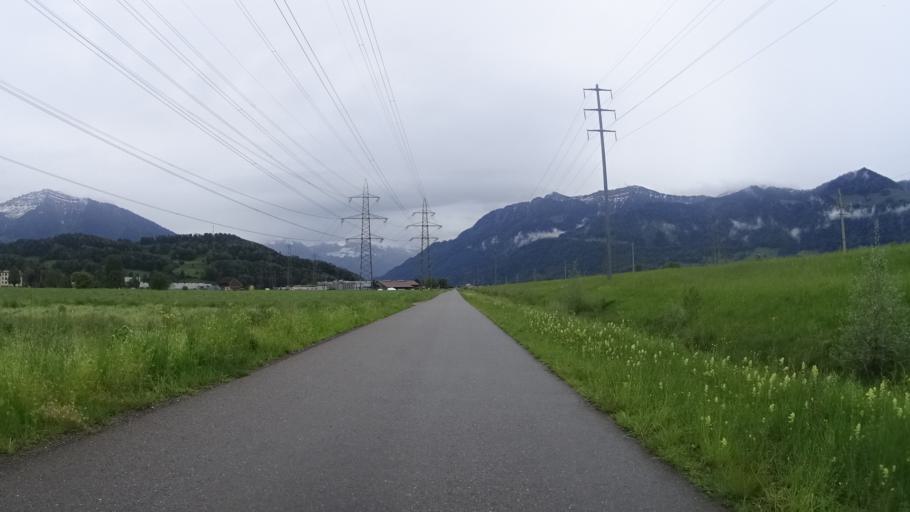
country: CH
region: Saint Gallen
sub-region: Wahlkreis See-Gaster
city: Benken
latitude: 47.1957
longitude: 8.9868
